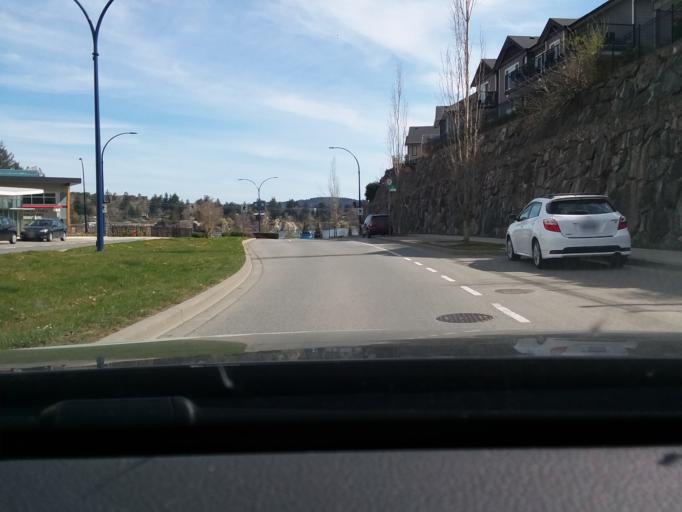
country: CA
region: British Columbia
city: Langford
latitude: 48.4450
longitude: -123.5342
